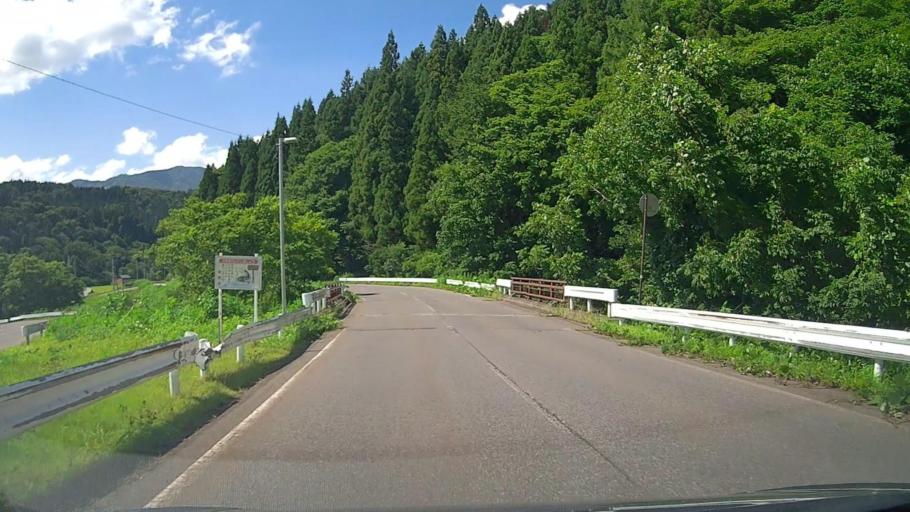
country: JP
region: Nagano
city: Iiyama
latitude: 36.9241
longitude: 138.4285
